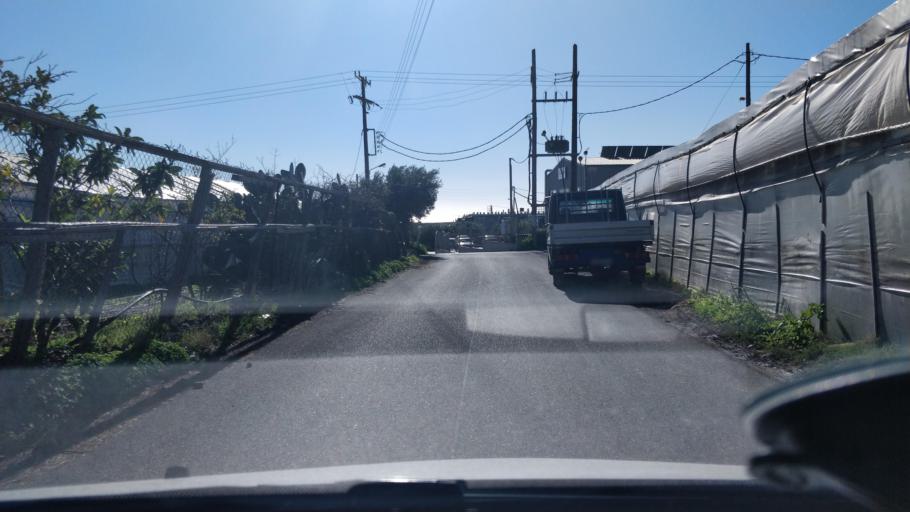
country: GR
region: Crete
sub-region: Nomos Lasithiou
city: Gra Liyia
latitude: 35.0156
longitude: 25.6765
